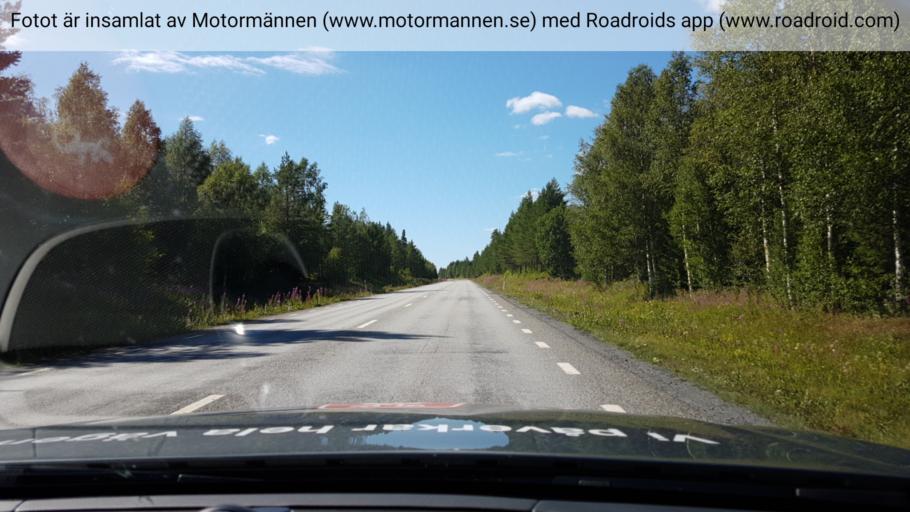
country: SE
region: Jaemtland
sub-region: Krokoms Kommun
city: Valla
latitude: 63.3086
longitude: 13.8315
